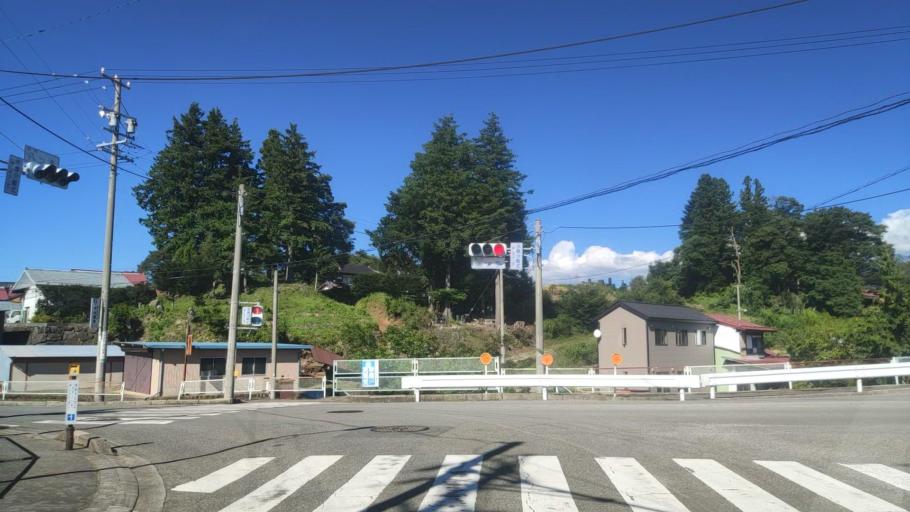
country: JP
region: Nagano
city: Chino
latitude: 35.9727
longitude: 138.2206
